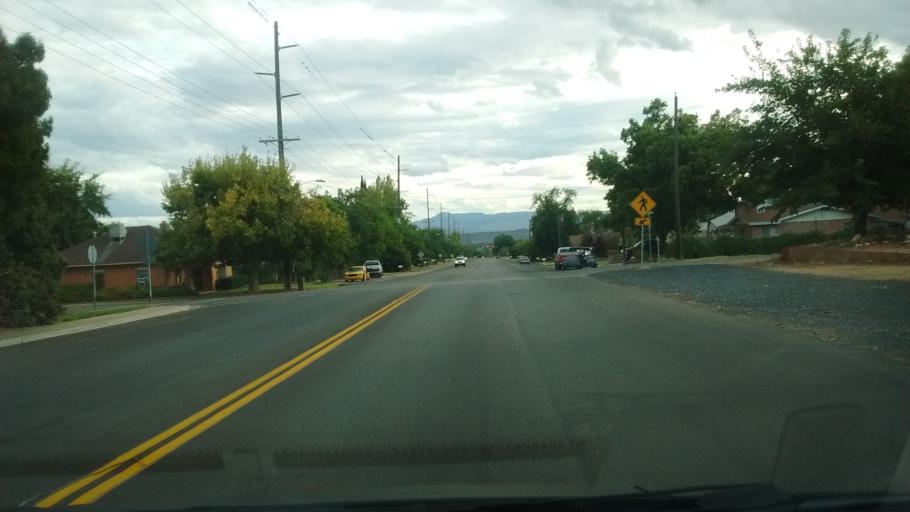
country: US
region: Utah
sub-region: Washington County
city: Washington
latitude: 37.1343
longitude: -113.5099
